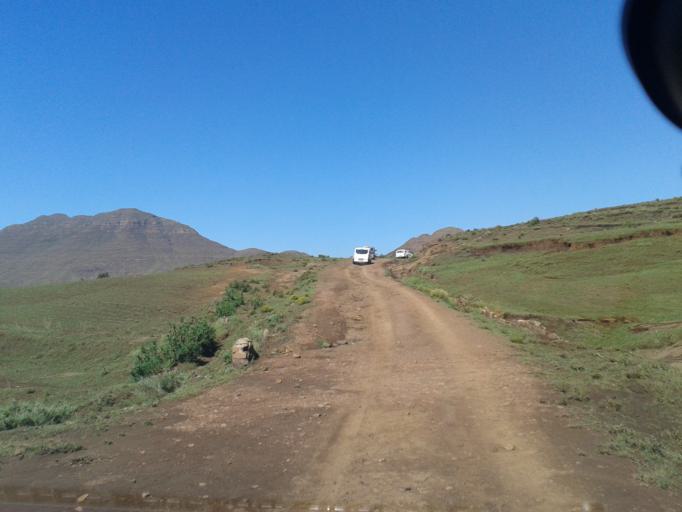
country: LS
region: Maseru
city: Nako
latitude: -29.8429
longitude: 27.5651
